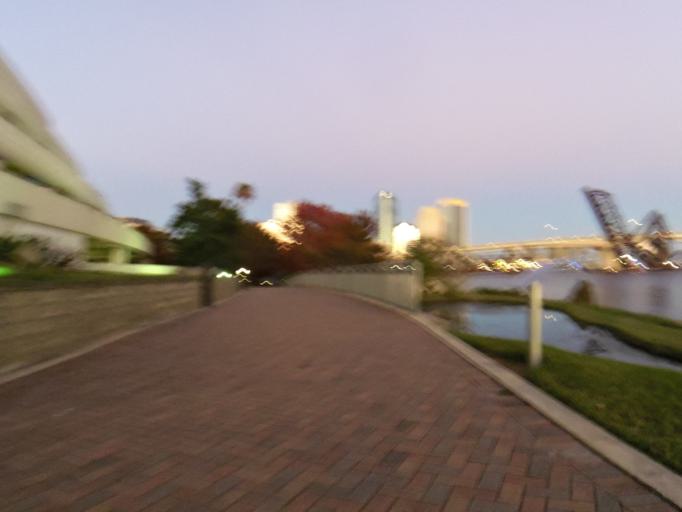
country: US
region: Florida
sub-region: Duval County
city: Jacksonville
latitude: 30.3231
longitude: -81.6737
